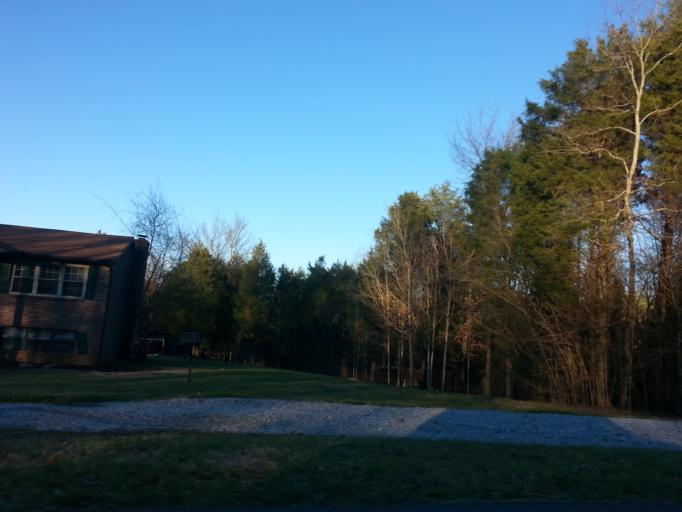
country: US
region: Tennessee
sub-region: Knox County
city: Knoxville
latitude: 35.9363
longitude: -83.8494
